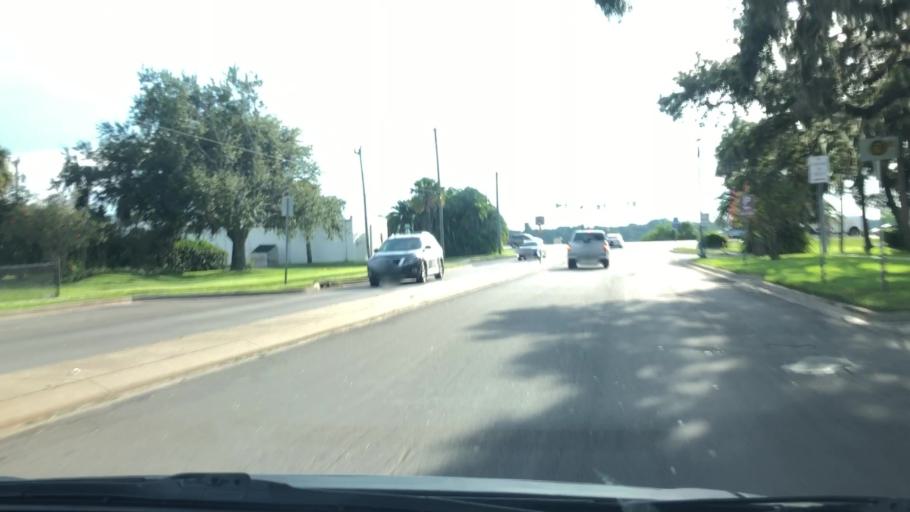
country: US
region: Florida
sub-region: Saint Johns County
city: Saint Augustine
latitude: 29.8992
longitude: -81.3187
